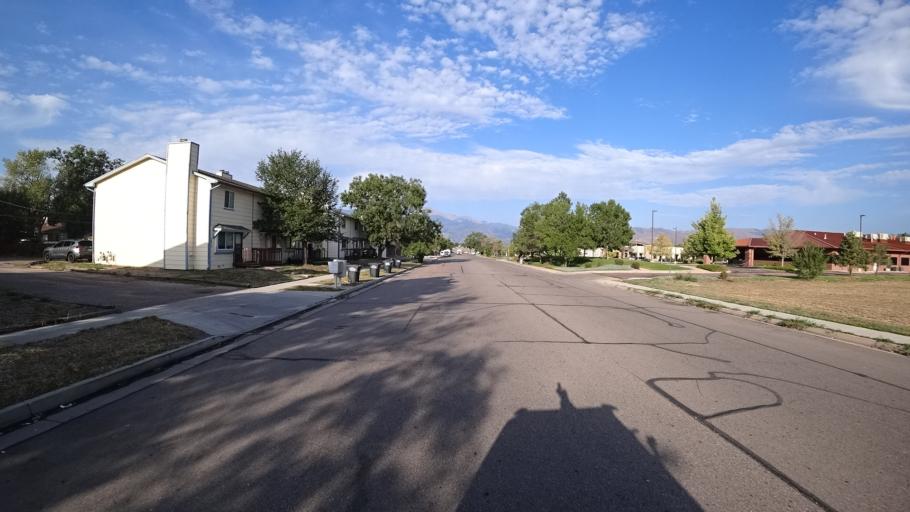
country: US
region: Colorado
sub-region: El Paso County
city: Colorado Springs
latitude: 38.8568
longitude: -104.7901
